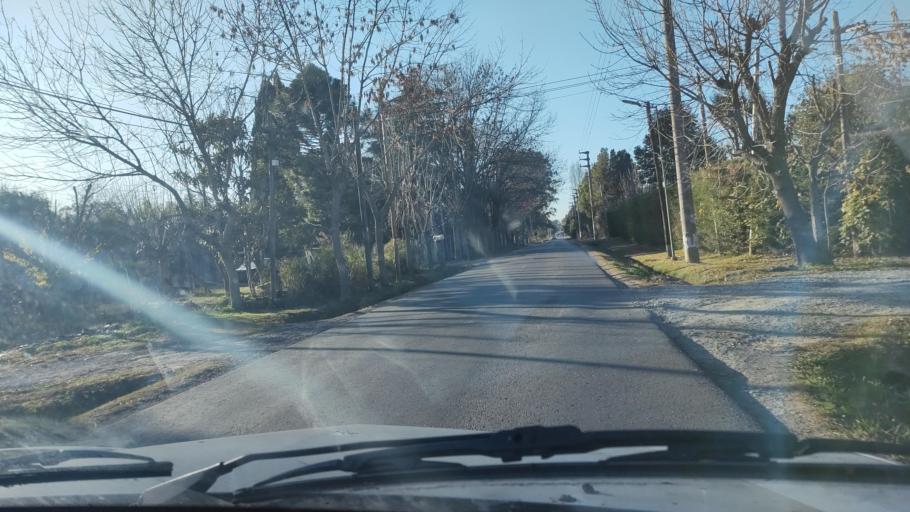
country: AR
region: Buenos Aires
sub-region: Partido de La Plata
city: La Plata
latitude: -34.9005
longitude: -58.0601
